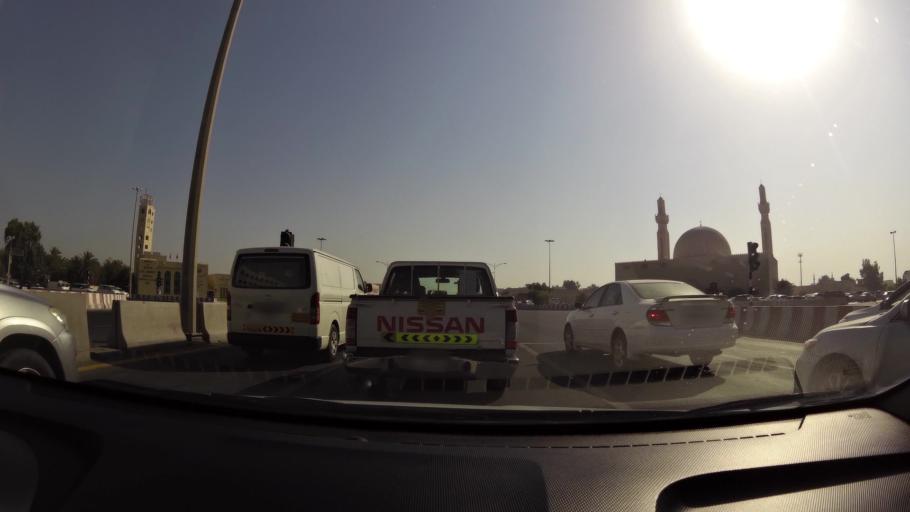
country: AE
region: Ash Shariqah
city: Sharjah
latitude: 25.3324
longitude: 55.4233
